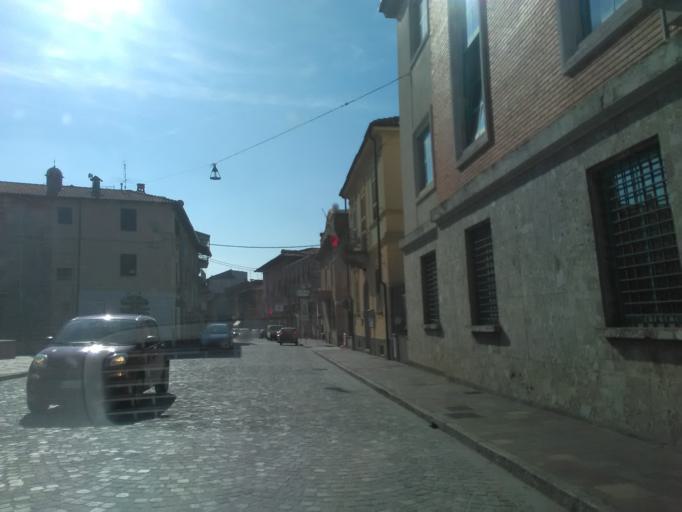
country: IT
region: Piedmont
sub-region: Provincia di Vercelli
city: Gattinara
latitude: 45.6175
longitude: 8.3709
